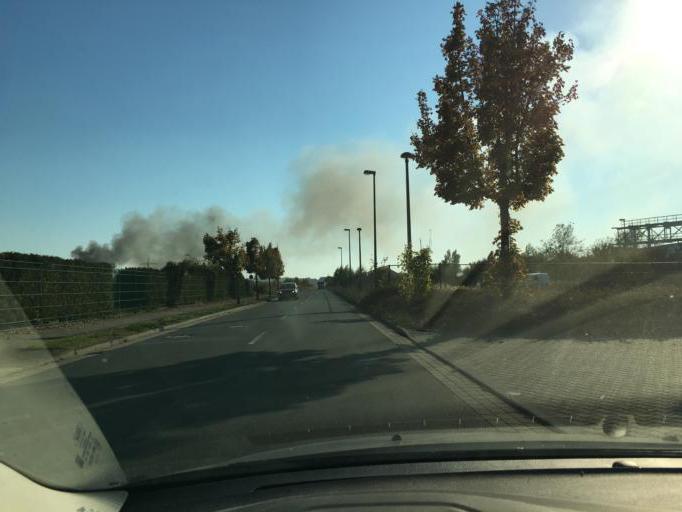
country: DE
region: Saxony
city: Bitterfeld-Wolfen
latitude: 51.6252
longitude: 12.3138
